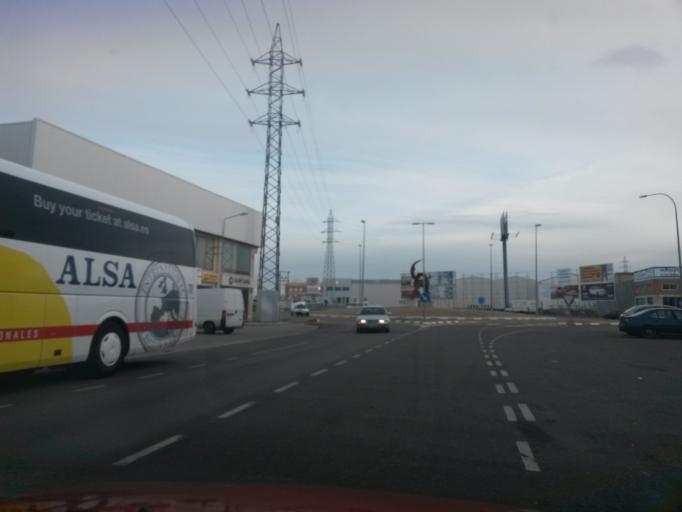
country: ES
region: Castille and Leon
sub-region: Provincia de Salamanca
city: Villares de la Reina
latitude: 40.9965
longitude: -5.6345
